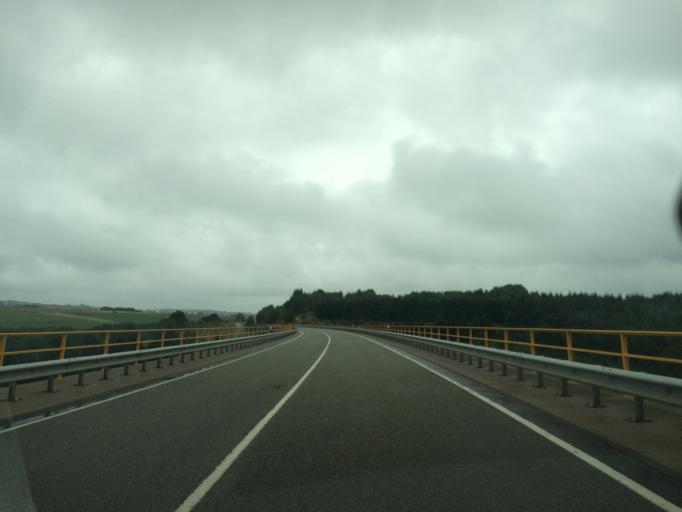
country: DE
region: Rheinland-Pfalz
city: Hoheischweiler
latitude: 49.2136
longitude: 7.5582
